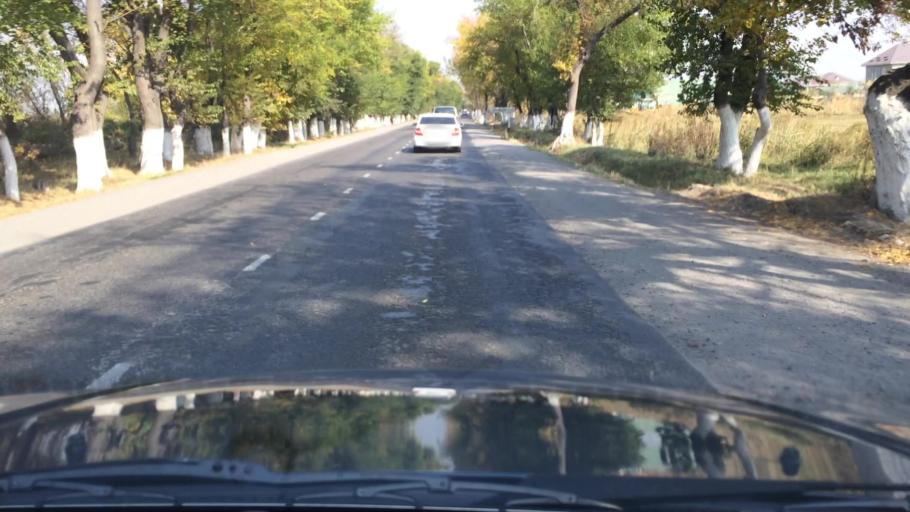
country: KG
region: Chuy
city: Lebedinovka
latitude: 42.9086
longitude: 74.6871
